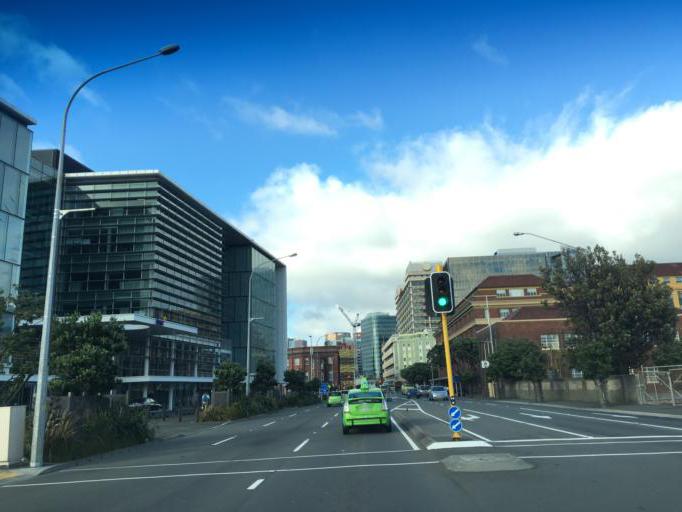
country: NZ
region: Wellington
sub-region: Wellington City
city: Wellington
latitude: -41.2785
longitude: 174.7821
